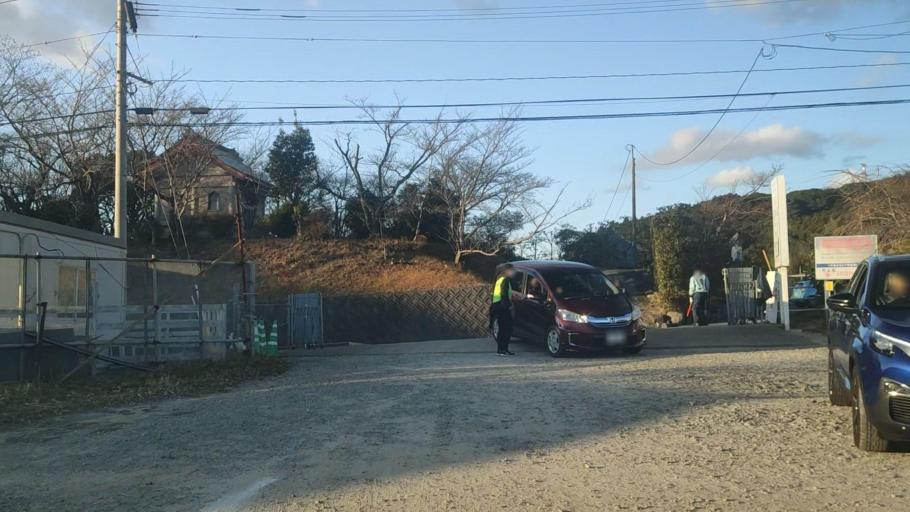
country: JP
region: Fukuoka
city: Dazaifu
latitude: 33.5276
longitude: 130.5480
